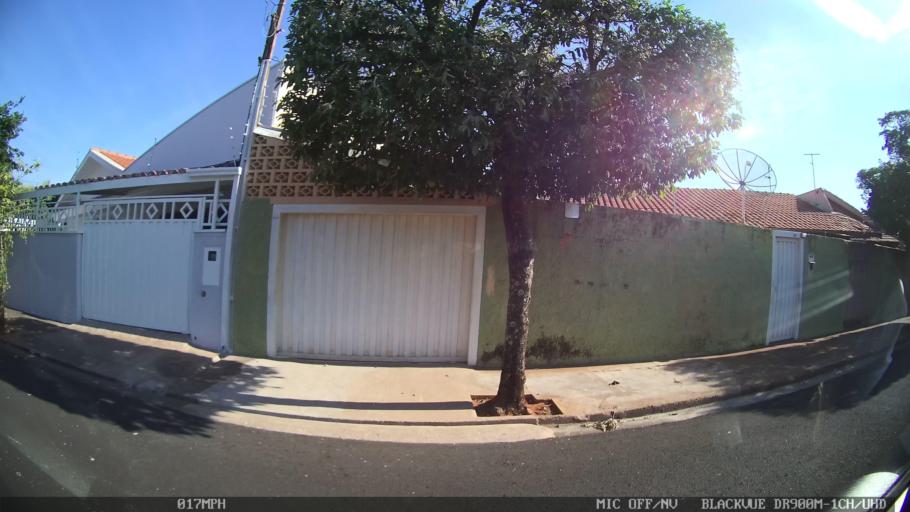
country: BR
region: Sao Paulo
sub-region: Sao Jose Do Rio Preto
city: Sao Jose do Rio Preto
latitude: -20.7808
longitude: -49.3653
